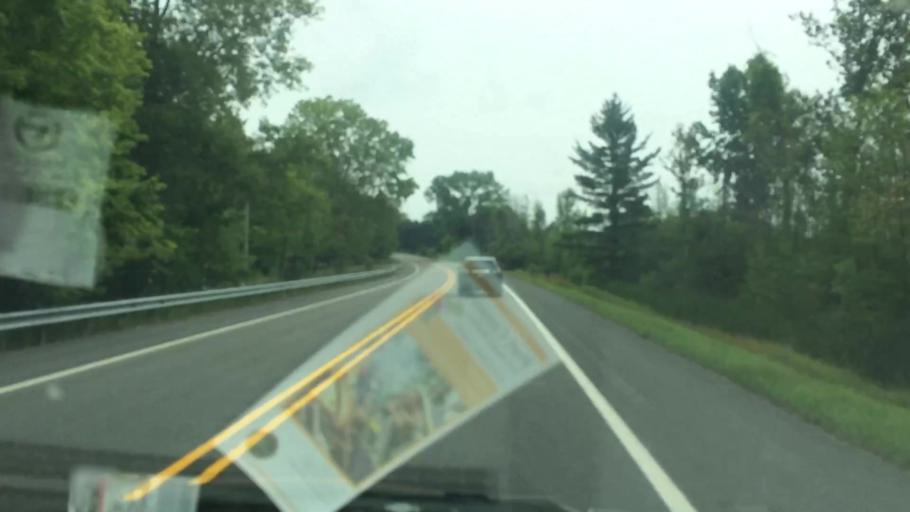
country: US
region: Michigan
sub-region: Huron County
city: Harbor Beach
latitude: 44.0224
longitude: -82.8157
